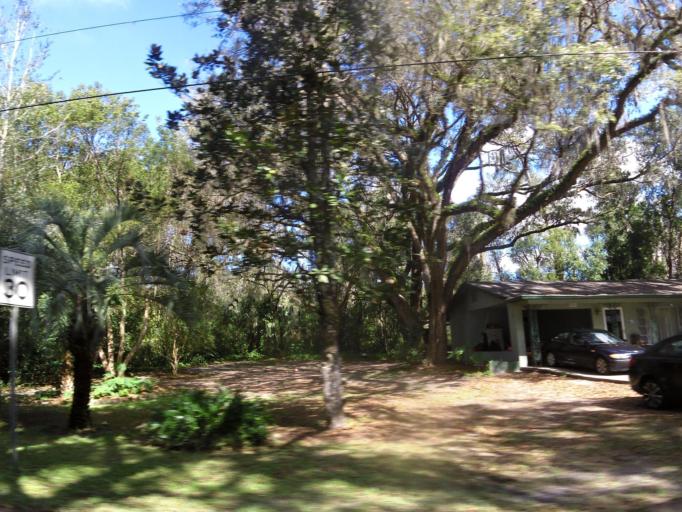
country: US
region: Florida
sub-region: Volusia County
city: Orange City
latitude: 28.9482
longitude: -81.3081
